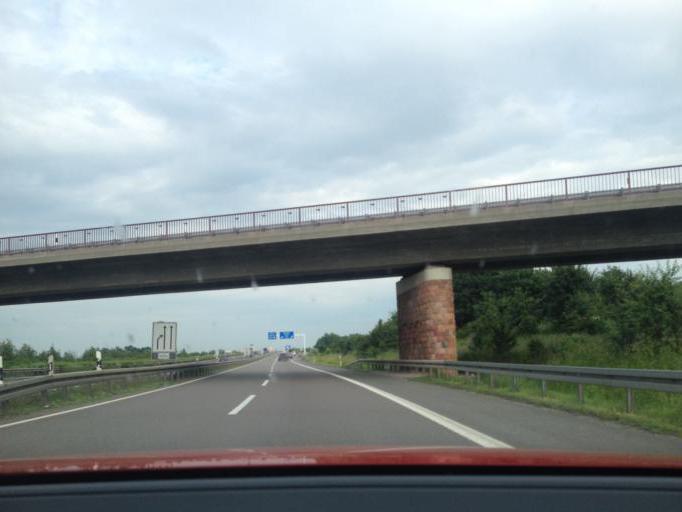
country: DE
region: Saxony
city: Wiedemar
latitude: 51.4295
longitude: 12.1881
